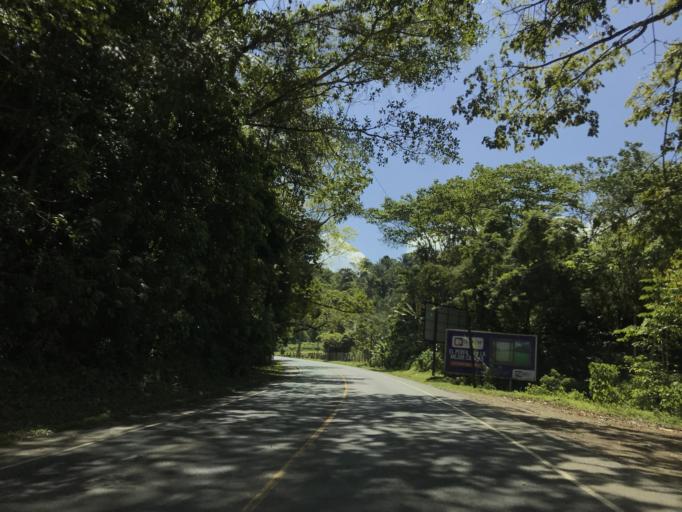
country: GT
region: Izabal
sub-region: Municipio de Puerto Barrios
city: Puerto Barrios
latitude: 15.6644
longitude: -88.5580
